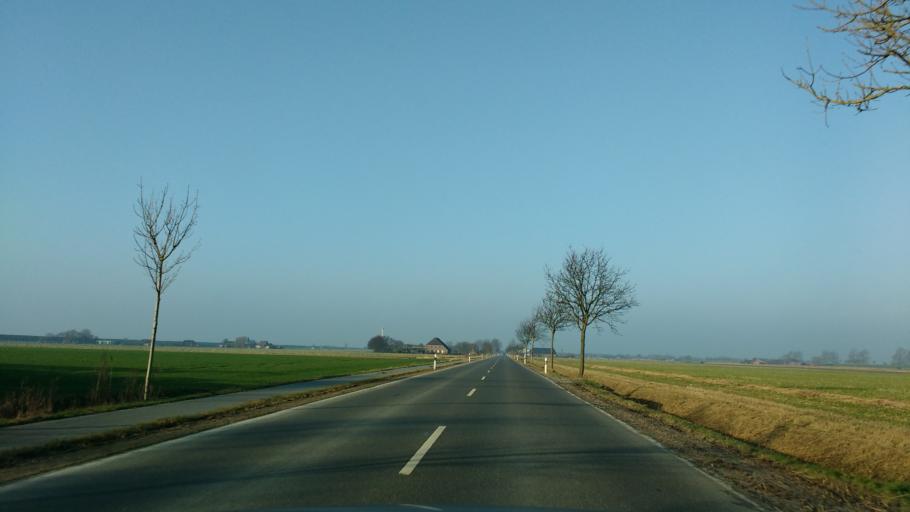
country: DE
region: Schleswig-Holstein
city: Friedrichskoog
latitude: 53.9890
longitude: 8.9081
